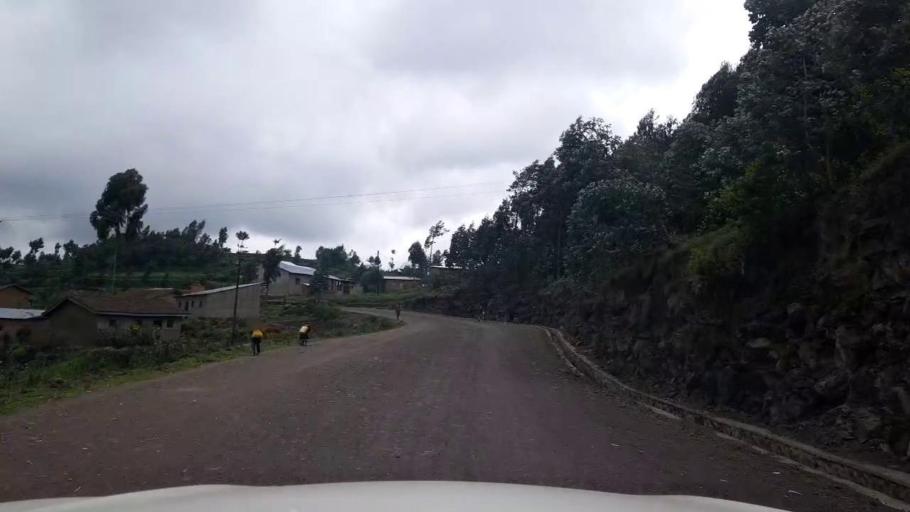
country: RW
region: Northern Province
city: Musanze
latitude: -1.5798
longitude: 29.4819
